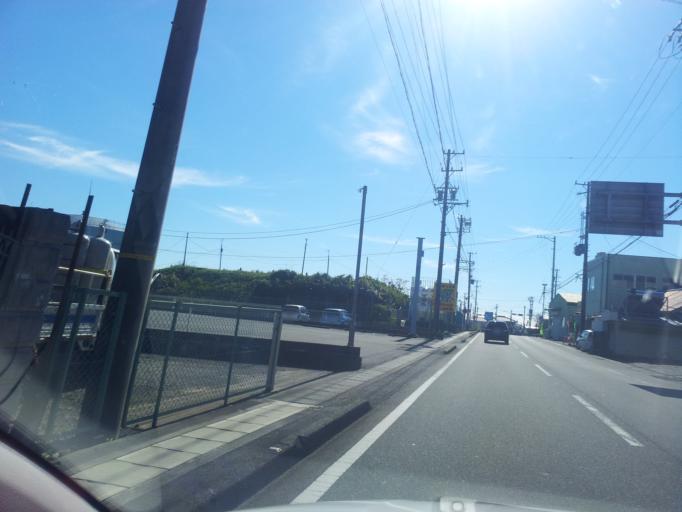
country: JP
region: Shizuoka
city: Kanaya
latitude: 34.8061
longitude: 138.1352
